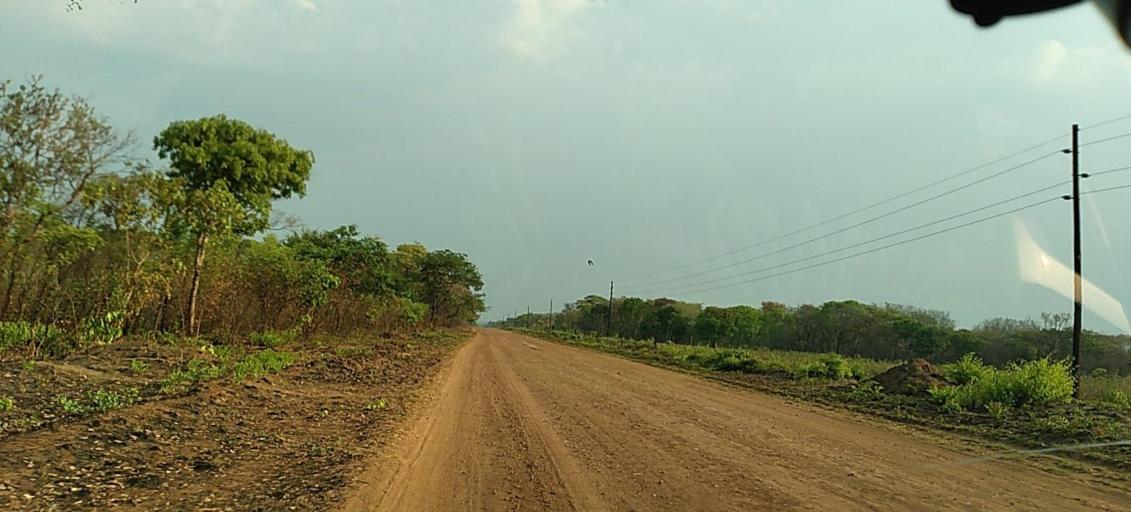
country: ZM
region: Western
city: Lukulu
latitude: -14.0011
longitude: 23.6177
